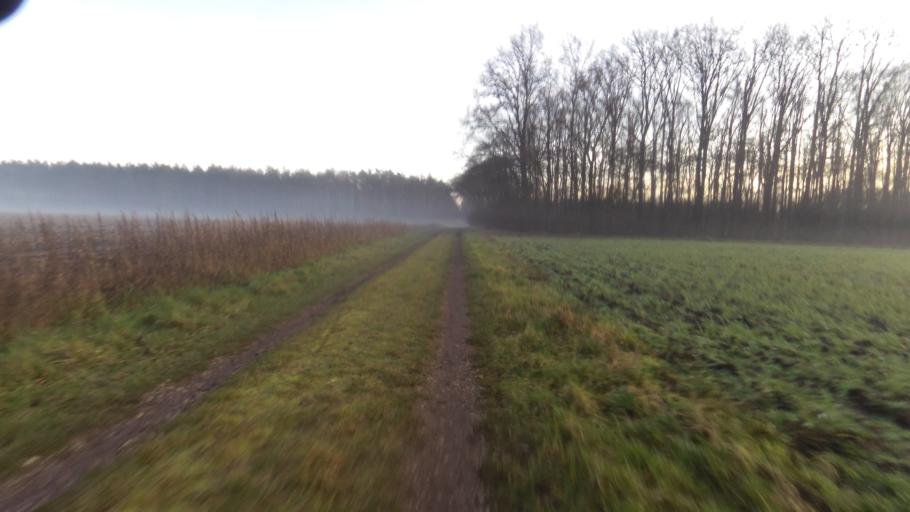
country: NL
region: Gelderland
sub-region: Gemeente Apeldoorn
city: Uddel
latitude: 52.2408
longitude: 5.7879
